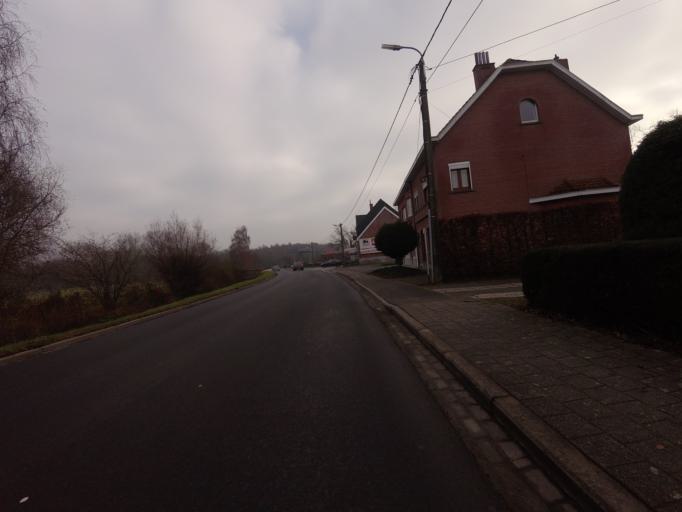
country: BE
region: Flanders
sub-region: Provincie Vlaams-Brabant
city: Galmaarden
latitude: 50.8045
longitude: 3.9631
